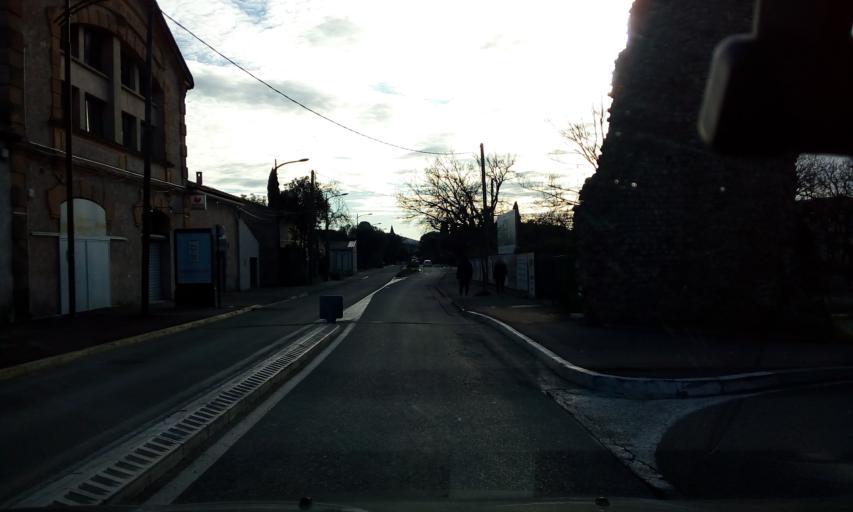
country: FR
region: Provence-Alpes-Cote d'Azur
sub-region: Departement du Var
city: Frejus
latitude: 43.4394
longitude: 6.7433
